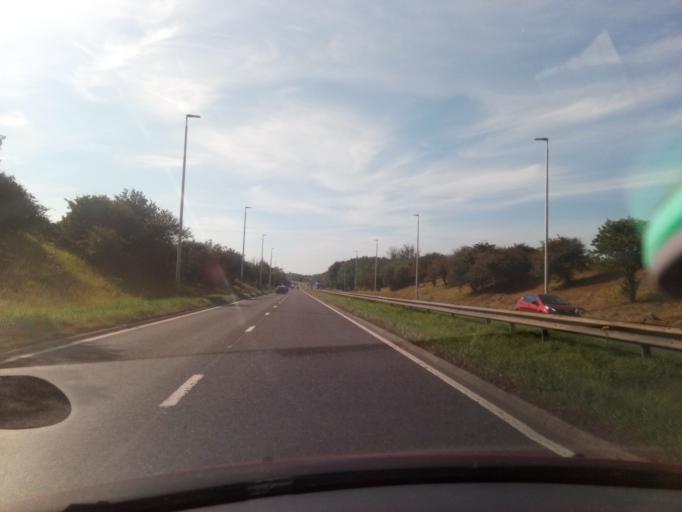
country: GB
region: England
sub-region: County Durham
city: Shotton
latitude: 54.7743
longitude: -1.3581
